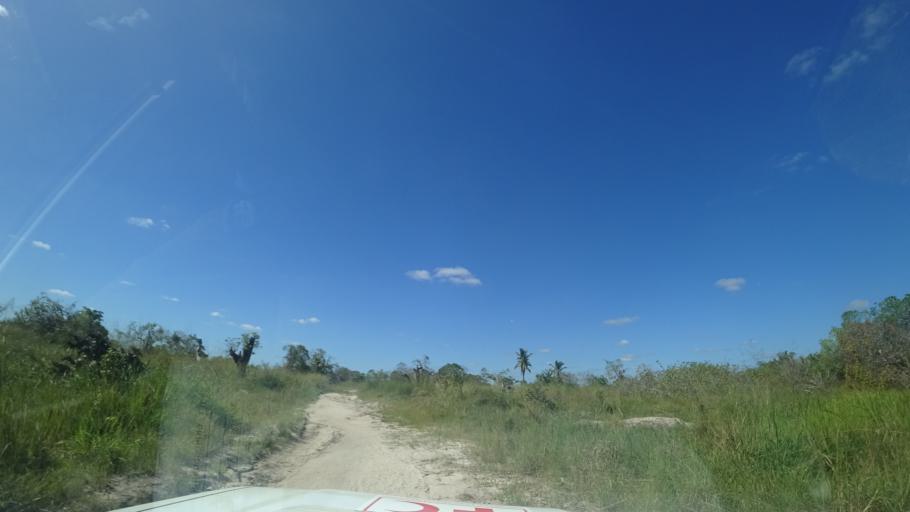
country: MZ
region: Sofala
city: Dondo
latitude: -19.4831
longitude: 34.6198
